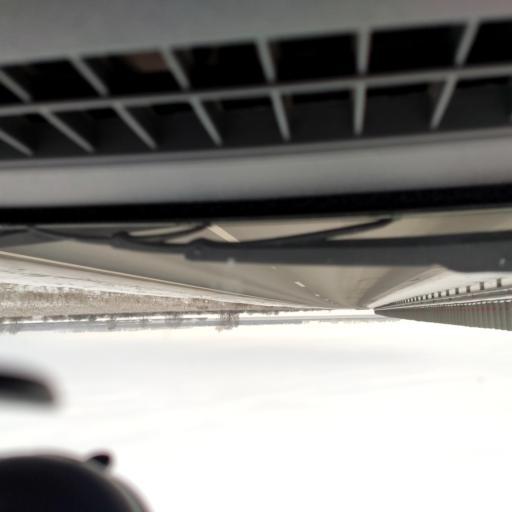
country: RU
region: Bashkortostan
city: Kushnarenkovo
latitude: 55.0672
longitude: 55.3549
